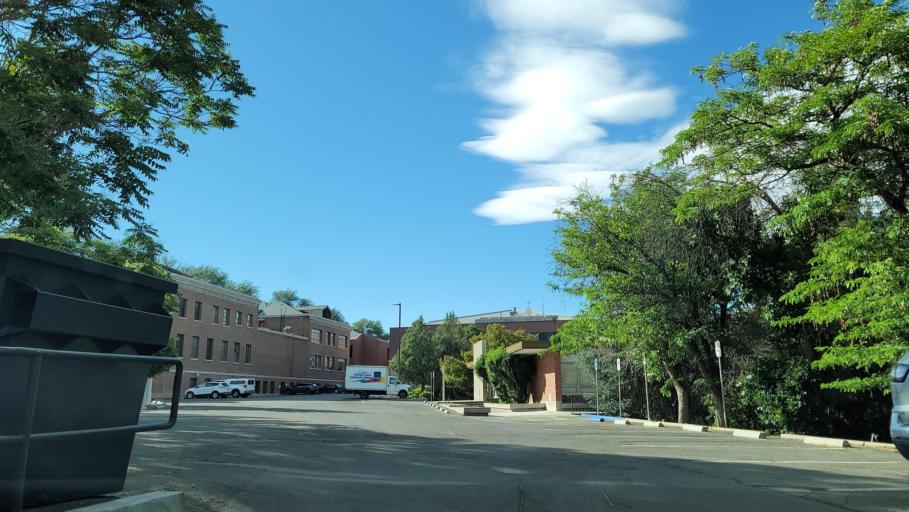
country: US
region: Nevada
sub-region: Washoe County
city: Reno
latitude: 39.5375
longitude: -119.8127
